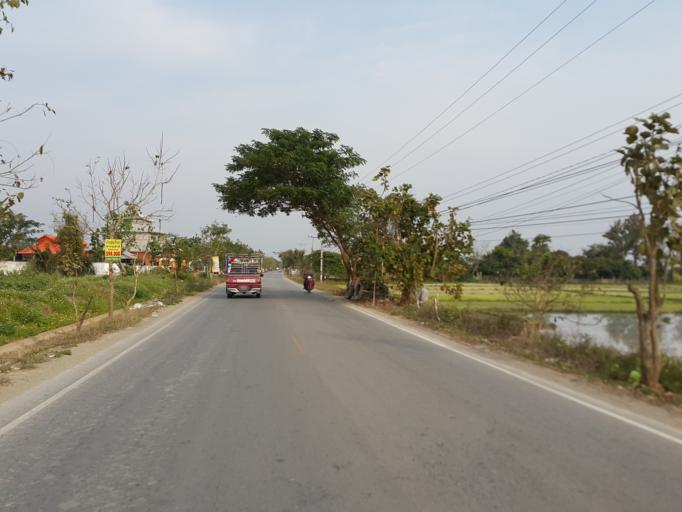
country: TH
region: Chiang Mai
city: Hang Dong
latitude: 18.6890
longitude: 98.9544
